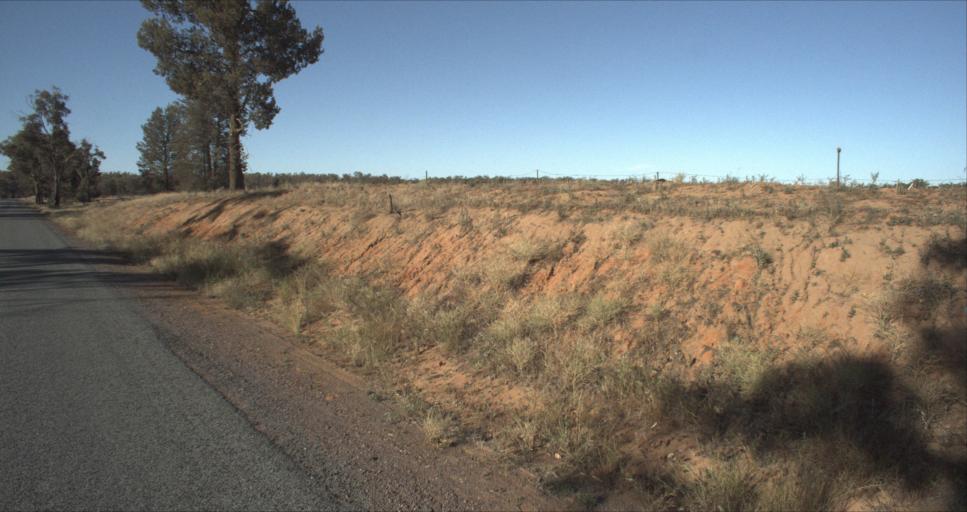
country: AU
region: New South Wales
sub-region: Leeton
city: Leeton
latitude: -34.6482
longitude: 146.3518
